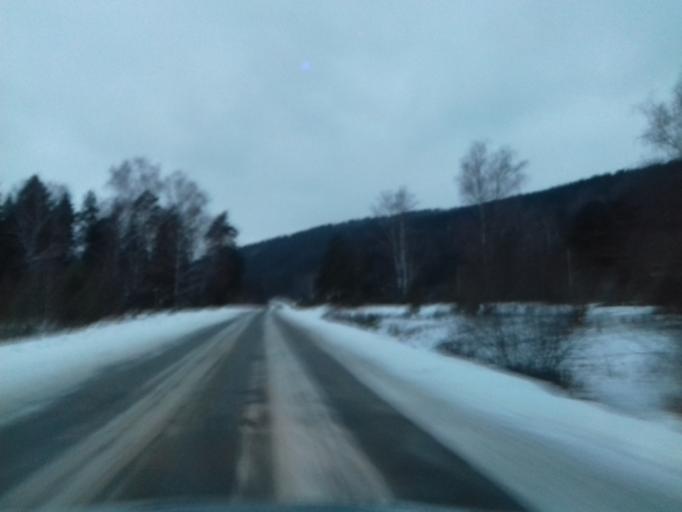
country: RU
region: Bashkortostan
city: Lomovka
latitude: 53.8637
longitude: 58.0215
